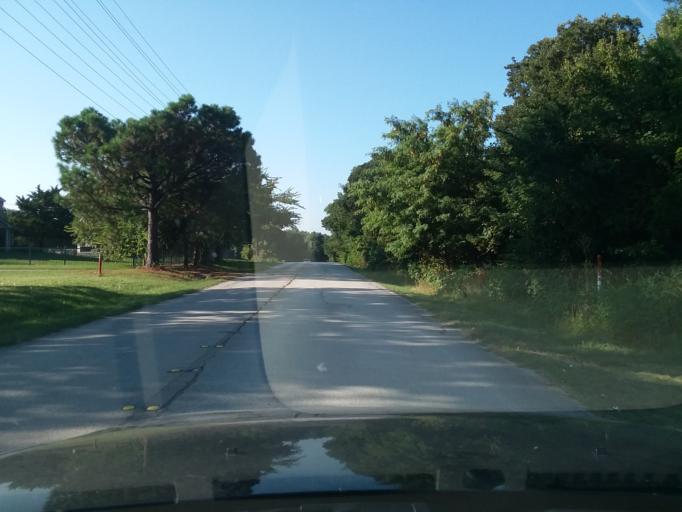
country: US
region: Texas
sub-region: Denton County
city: Copper Canyon
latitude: 33.1076
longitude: -97.0877
